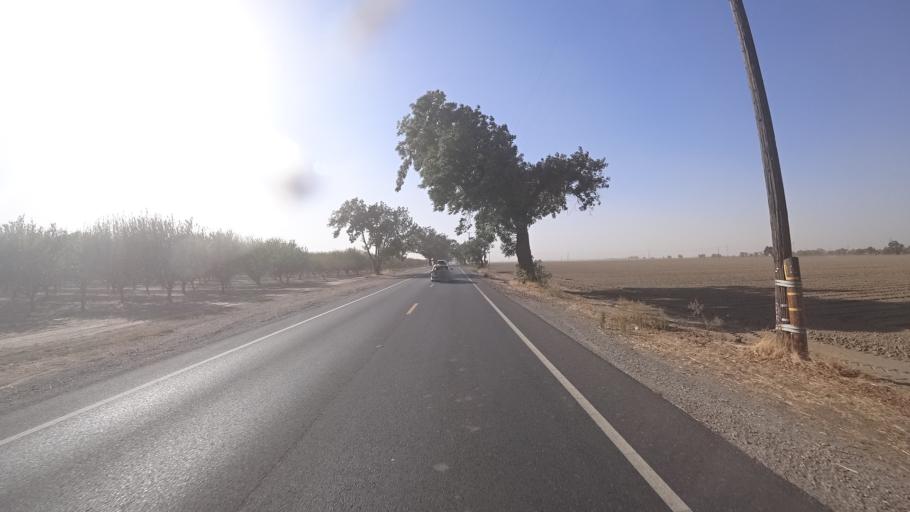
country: US
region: California
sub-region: Yolo County
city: Woodland
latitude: 38.7927
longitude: -121.7425
